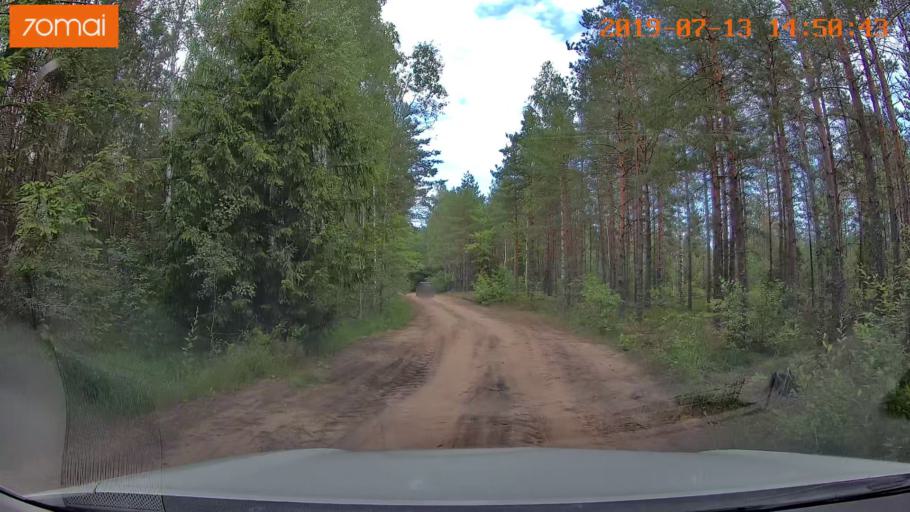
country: BY
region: Mogilev
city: Asipovichy
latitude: 53.2091
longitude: 28.7500
